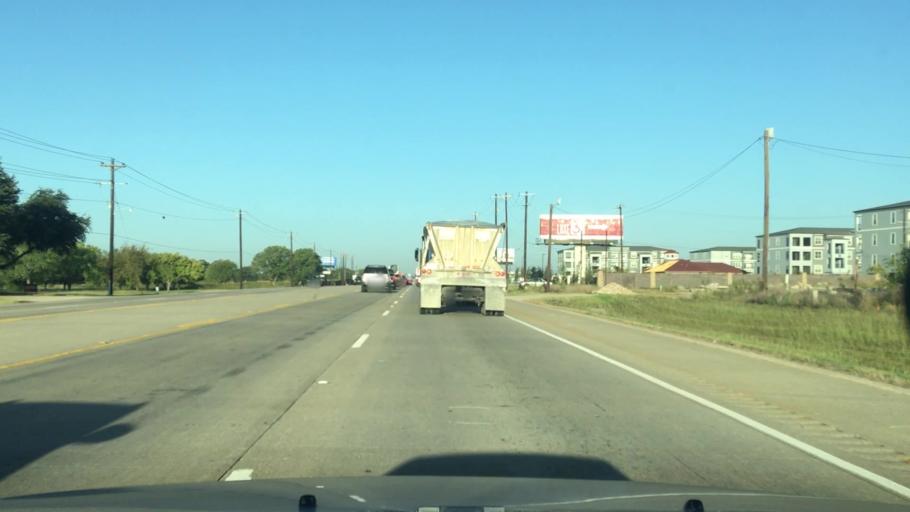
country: US
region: Texas
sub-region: Denton County
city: Cross Roads
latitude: 33.2232
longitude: -96.9714
